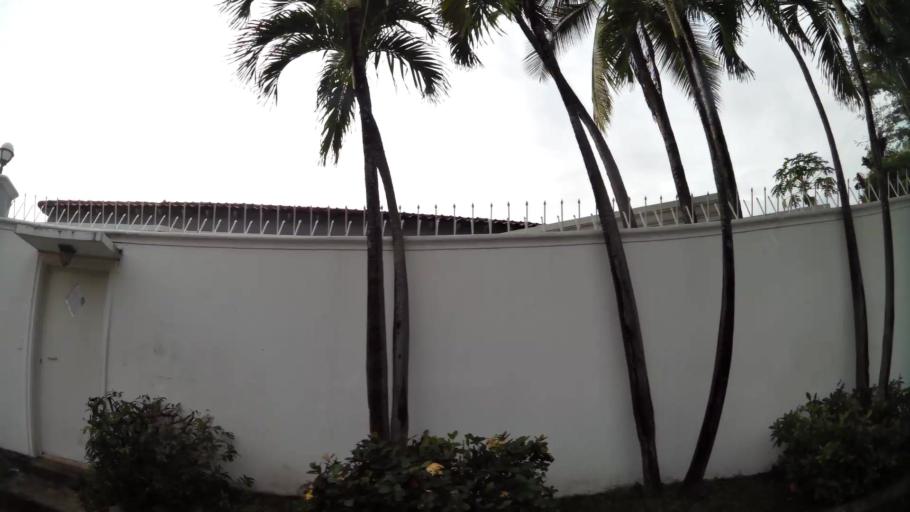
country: PA
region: Panama
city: Panama
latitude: 8.9988
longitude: -79.5009
